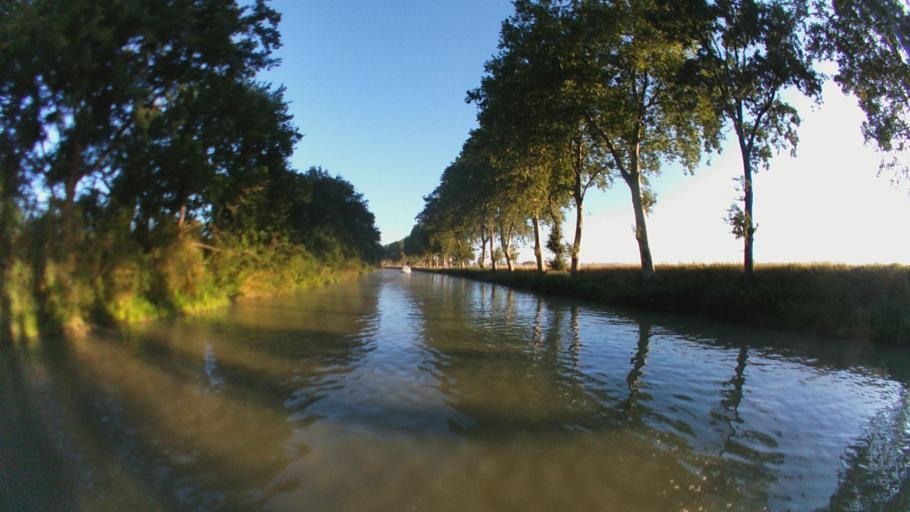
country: FR
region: Midi-Pyrenees
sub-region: Departement de la Haute-Garonne
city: Gardouch
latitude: 43.4091
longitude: 1.6636
